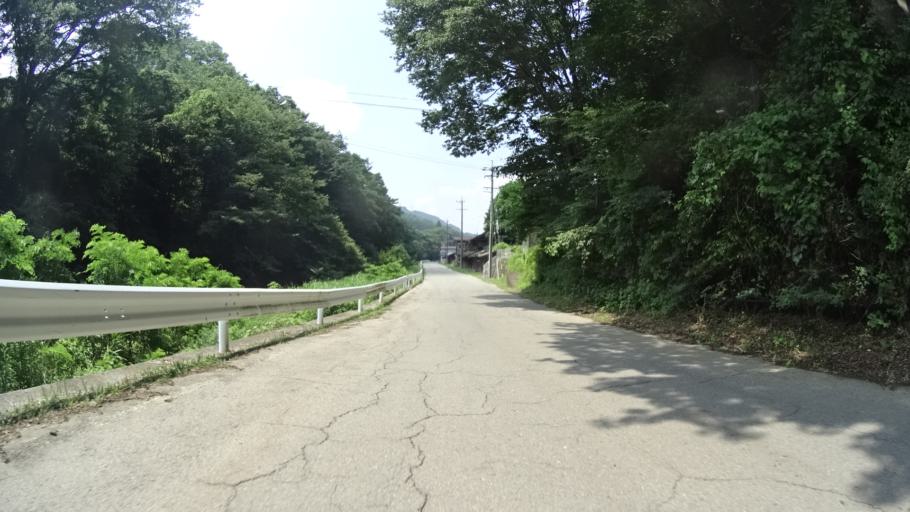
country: JP
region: Nagano
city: Saku
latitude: 36.1276
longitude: 138.5836
